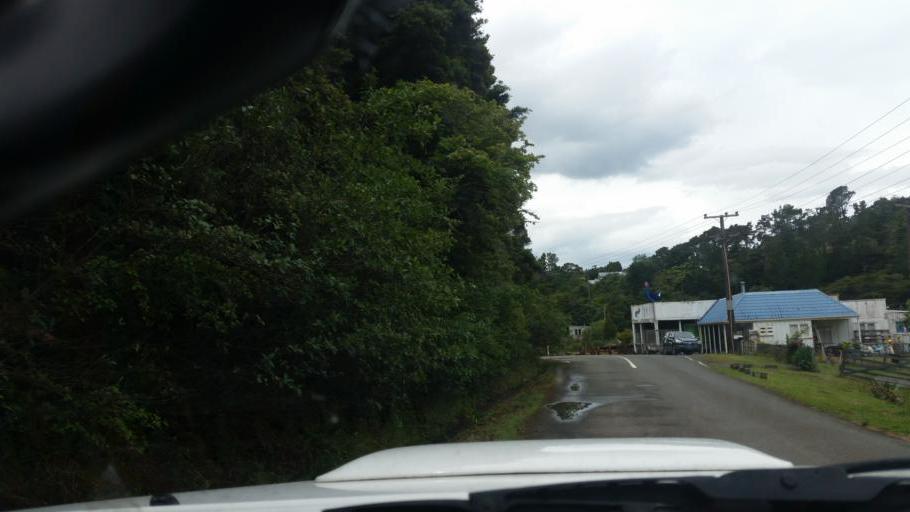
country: NZ
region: Northland
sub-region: Kaipara District
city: Dargaville
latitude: -35.7110
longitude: 173.6172
